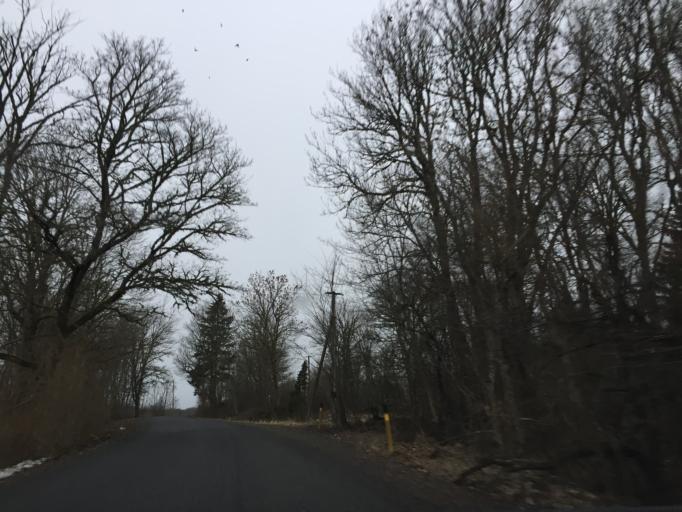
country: EE
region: Laeaene
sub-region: Lihula vald
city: Lihula
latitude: 58.6554
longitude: 23.6013
